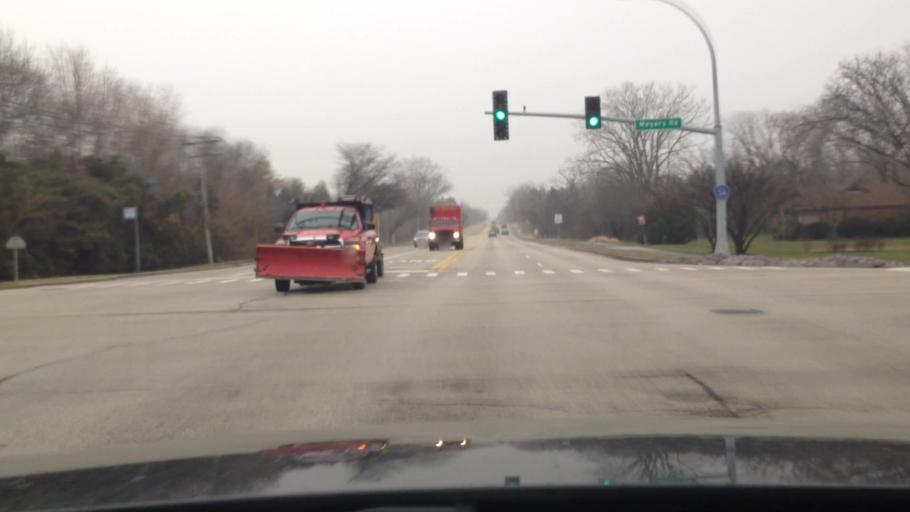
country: US
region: Illinois
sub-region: DuPage County
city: Downers Grove
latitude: 41.8314
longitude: -87.9915
